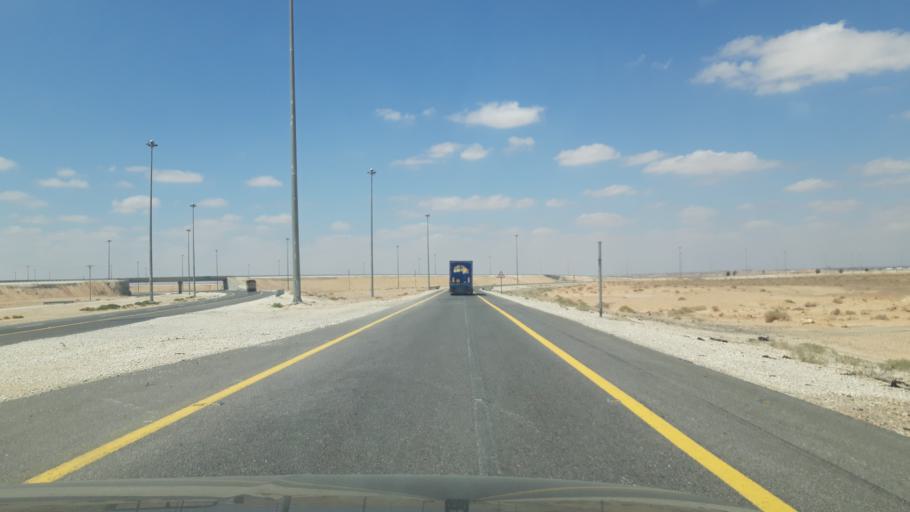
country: JO
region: Amman
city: Al Azraq ash Shamali
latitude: 31.7813
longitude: 36.7935
